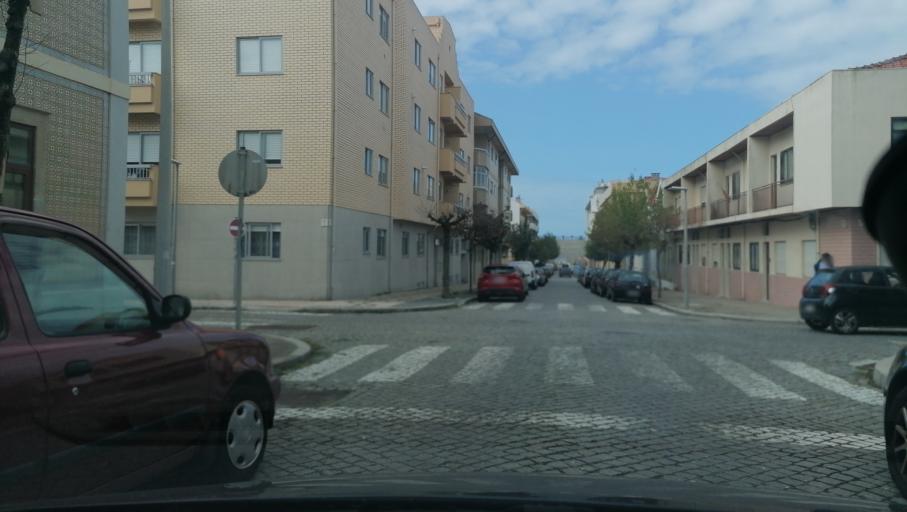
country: PT
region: Aveiro
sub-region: Espinho
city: Espinho
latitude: 41.0031
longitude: -8.6412
